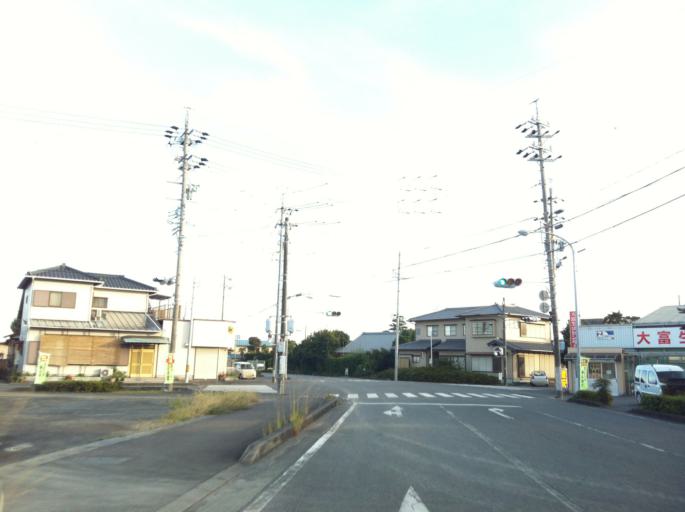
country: JP
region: Shizuoka
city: Yaizu
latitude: 34.8378
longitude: 138.2962
